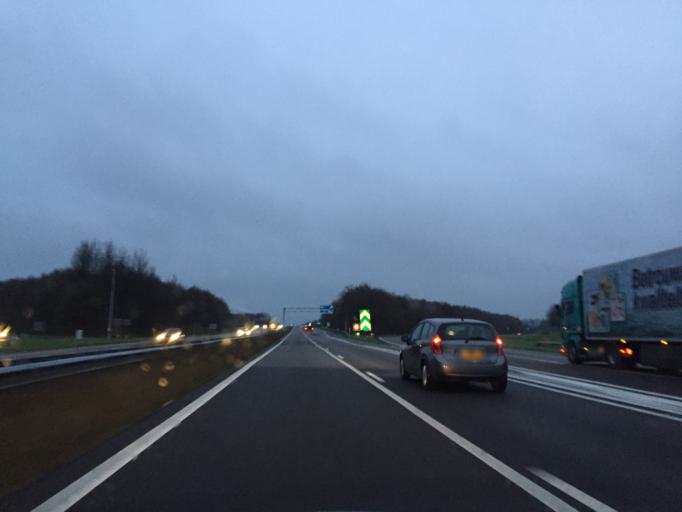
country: NL
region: North Brabant
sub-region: Roosendaal
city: Roosendaal
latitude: 51.5257
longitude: 4.4271
